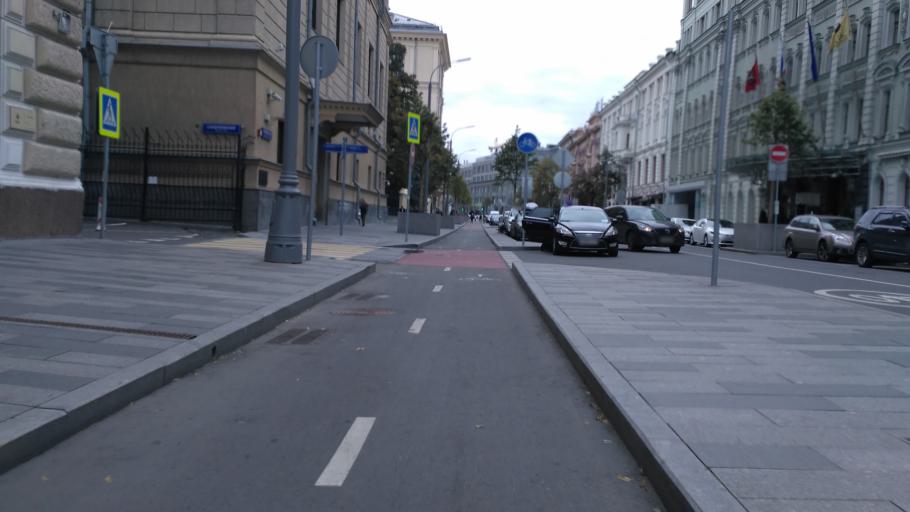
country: RU
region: Moscow
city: Moscow
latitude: 55.7640
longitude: 37.6200
